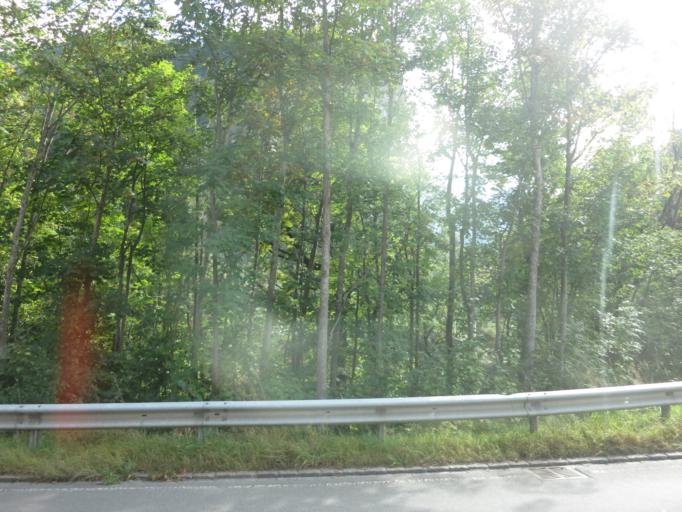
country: CH
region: Grisons
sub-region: Hinterrhein District
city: Thusis
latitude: 46.6938
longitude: 9.4403
